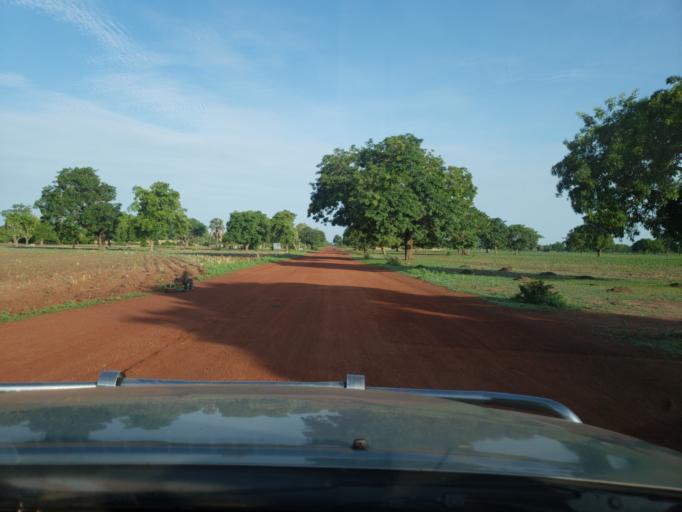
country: ML
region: Sikasso
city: Koutiala
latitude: 12.4160
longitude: -5.5698
